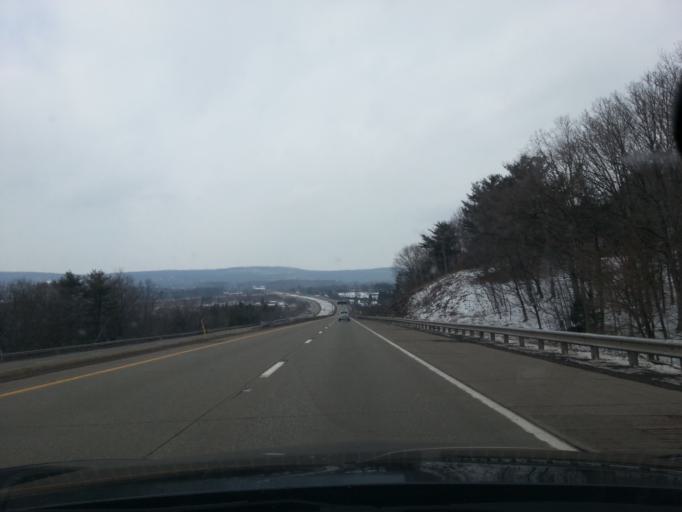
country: US
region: Pennsylvania
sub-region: Luzerne County
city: Conyngham
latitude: 41.0198
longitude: -76.0097
